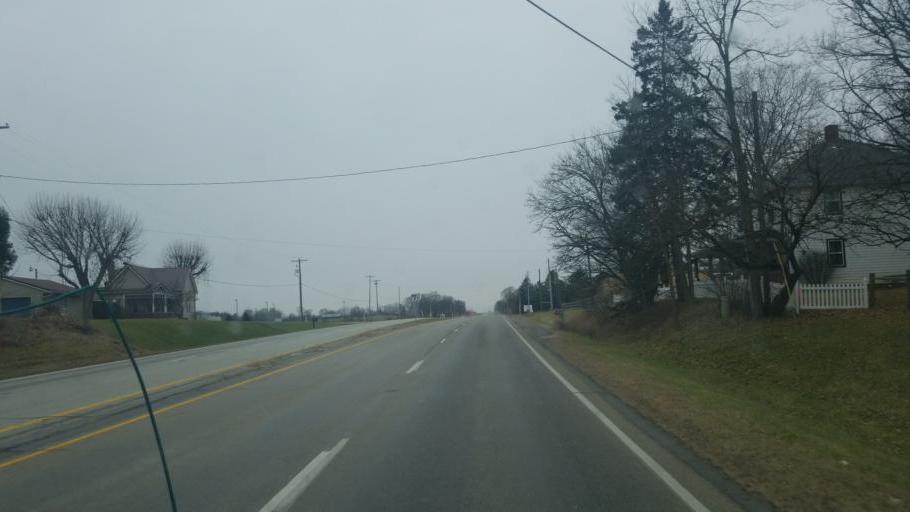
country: US
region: Indiana
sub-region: Henry County
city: Knightstown
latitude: 39.7943
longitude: -85.5394
